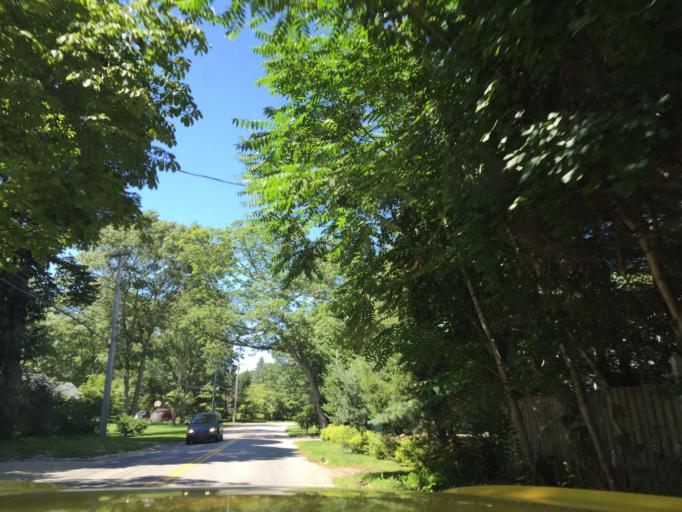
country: US
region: New York
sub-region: Suffolk County
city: Amagansett
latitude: 40.9999
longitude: -72.1330
